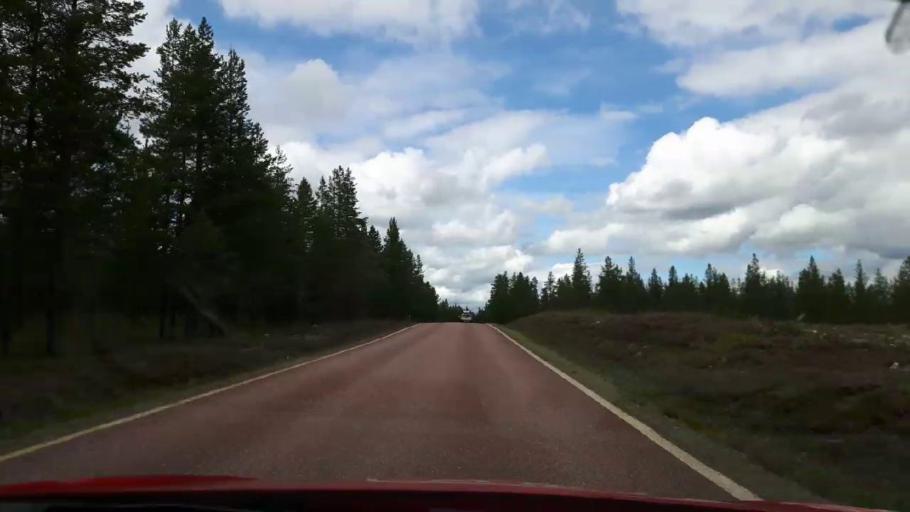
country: NO
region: Hedmark
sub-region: Trysil
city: Innbygda
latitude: 61.8534
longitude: 12.9498
